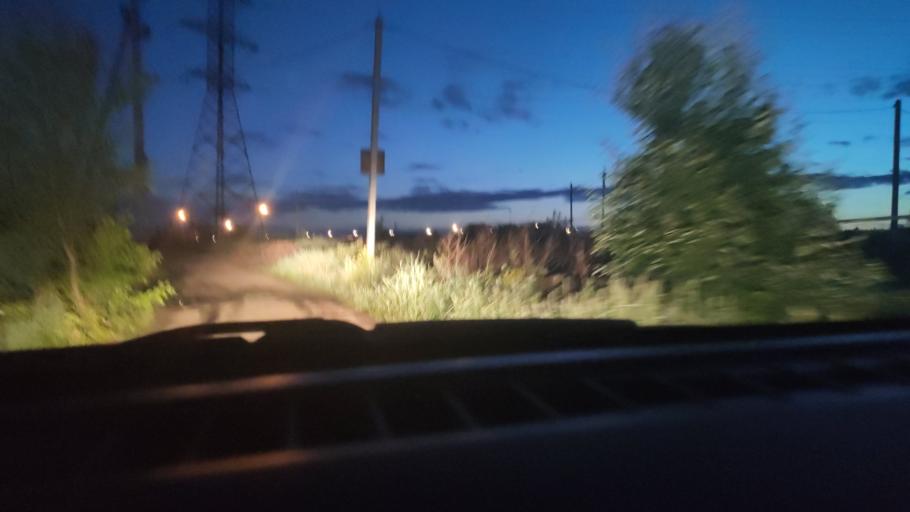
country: RU
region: Perm
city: Froly
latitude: 57.9278
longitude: 56.2748
